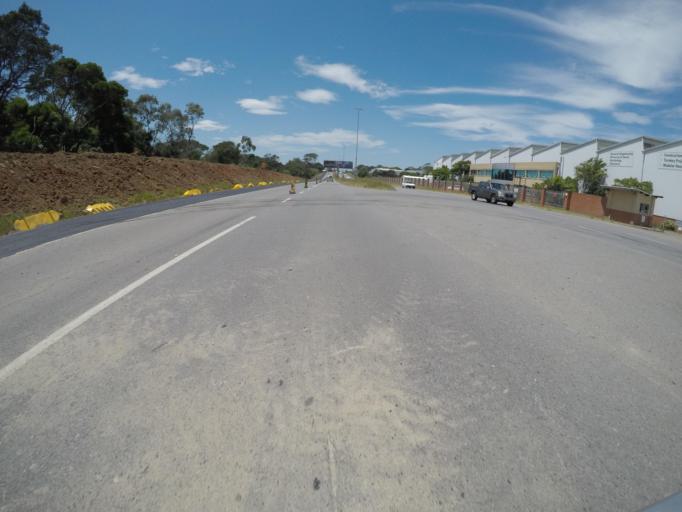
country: ZA
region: Eastern Cape
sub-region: Buffalo City Metropolitan Municipality
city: East London
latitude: -33.0361
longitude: 27.8367
